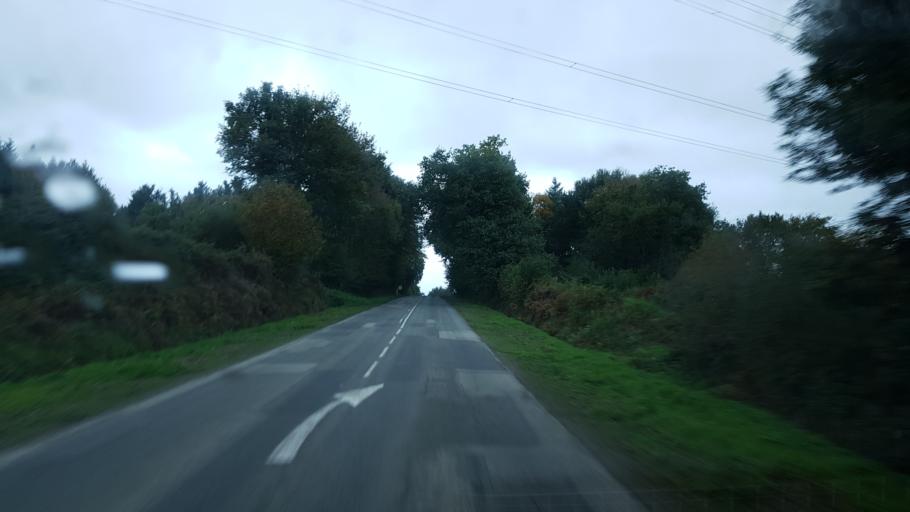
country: FR
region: Brittany
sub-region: Departement du Morbihan
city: Elven
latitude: 47.7434
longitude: -2.5712
